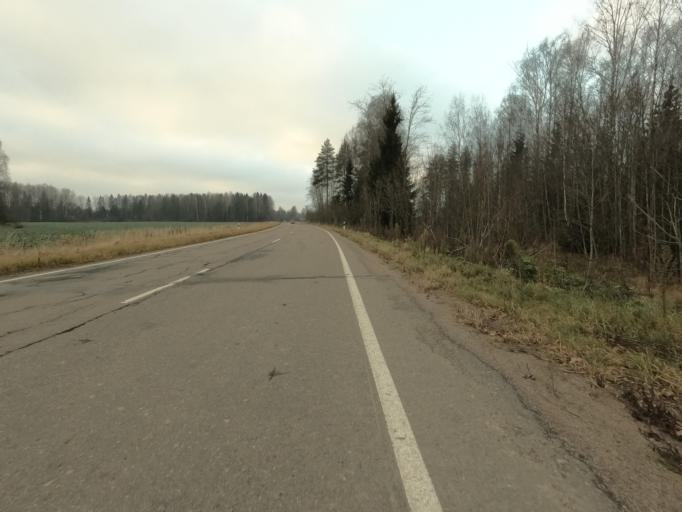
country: RU
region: Leningrad
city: Kirovsk
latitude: 59.8006
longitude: 30.9981
